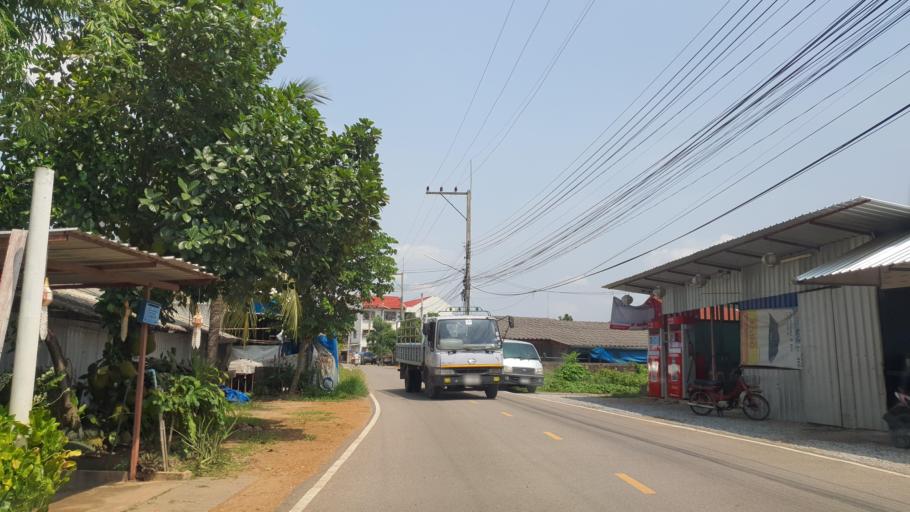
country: TH
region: Lamphun
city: Lamphun
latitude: 18.6027
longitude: 99.0280
